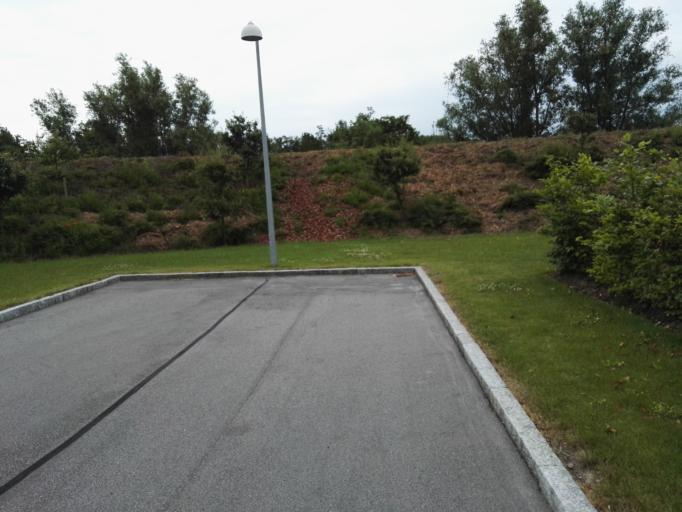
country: DK
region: Capital Region
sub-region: Egedal Kommune
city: Olstykke
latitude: 55.7847
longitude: 12.1419
